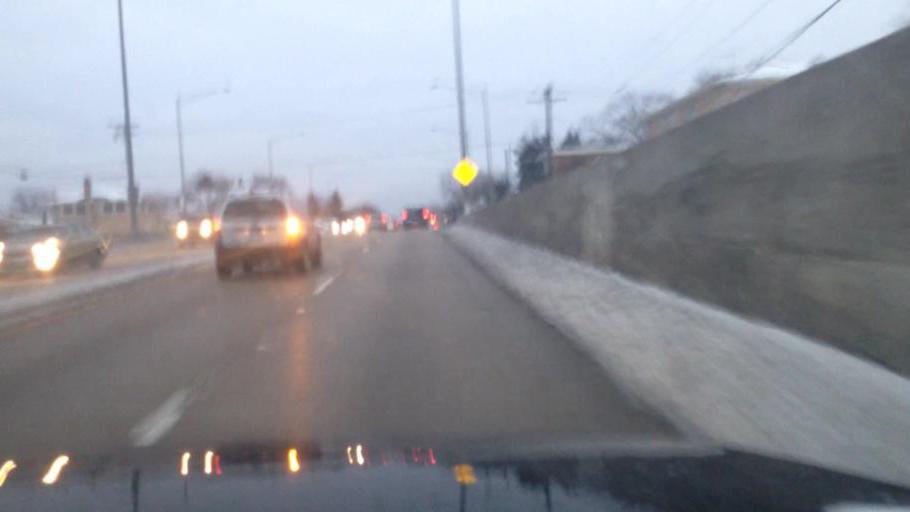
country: US
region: Illinois
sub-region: Cook County
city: Niles
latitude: 42.0404
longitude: -87.8248
